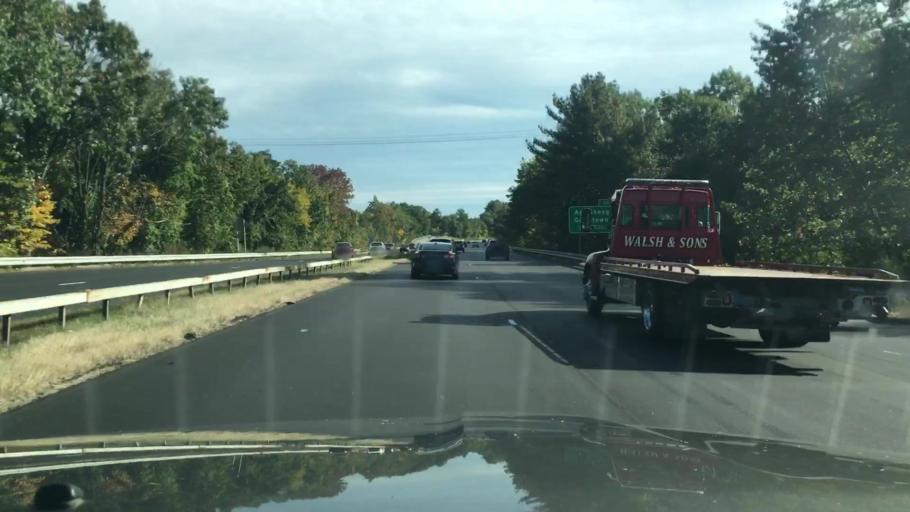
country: US
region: New Hampshire
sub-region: Hillsborough County
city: Manchester
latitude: 43.0112
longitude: -71.4774
